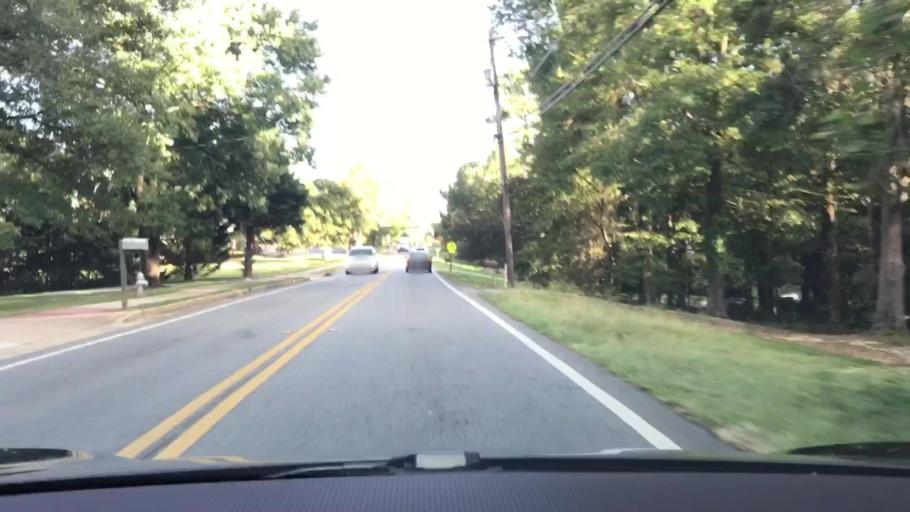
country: US
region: Georgia
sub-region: Gwinnett County
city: Dacula
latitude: 33.9957
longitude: -83.9015
